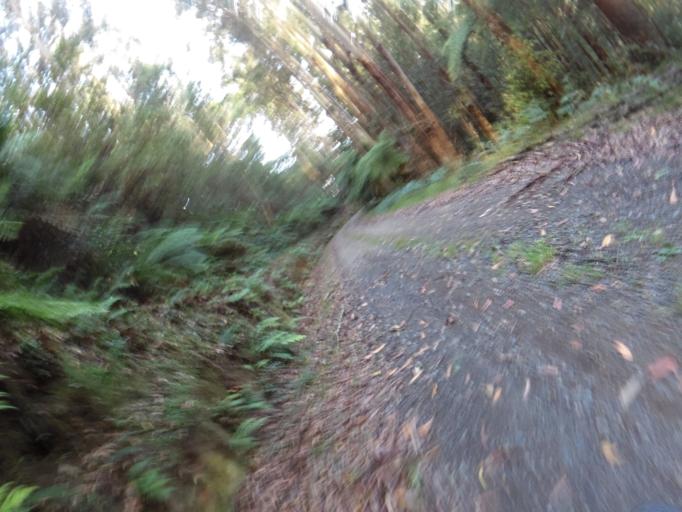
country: AU
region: Victoria
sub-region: Yarra Ranges
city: Millgrove
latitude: -37.8522
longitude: 145.8027
